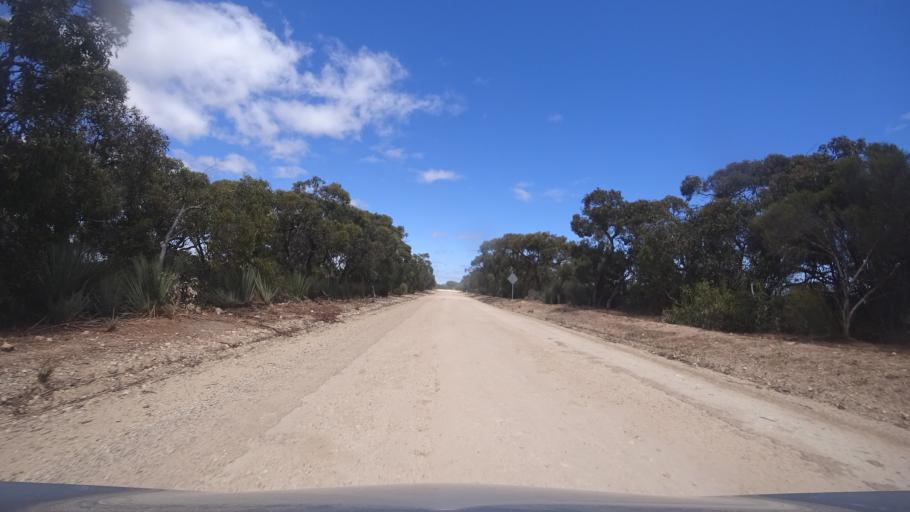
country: AU
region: South Australia
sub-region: Kangaroo Island
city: Kingscote
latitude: -35.6365
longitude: 137.2455
